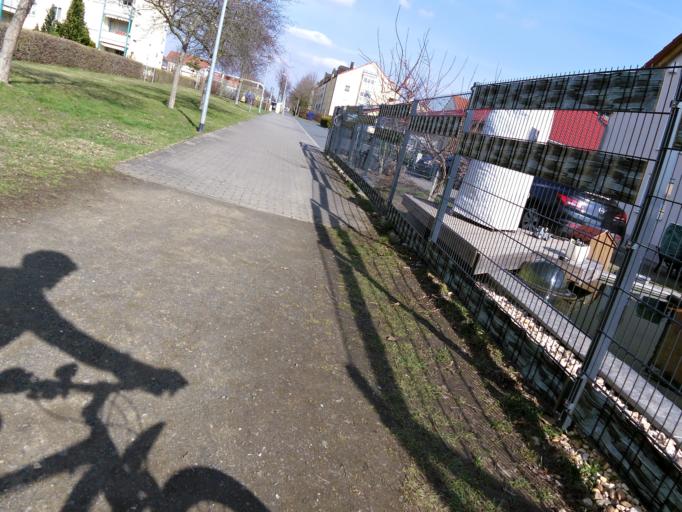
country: DE
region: Saxony
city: Markranstadt
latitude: 51.3005
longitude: 12.2651
